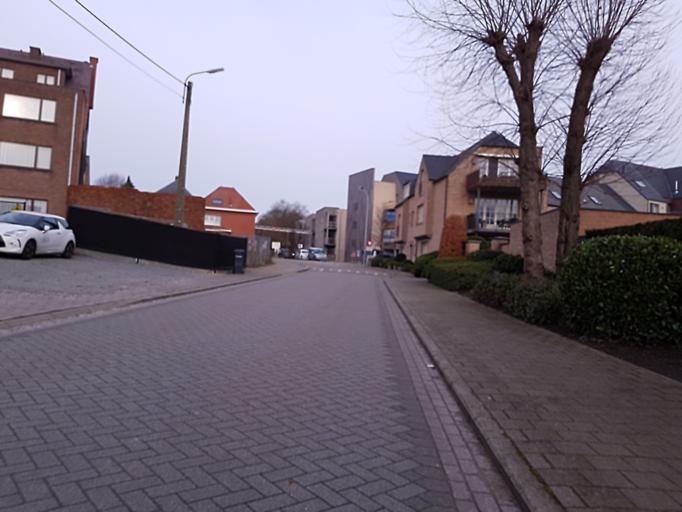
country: BE
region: Flanders
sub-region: Provincie Antwerpen
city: Putte
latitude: 51.0575
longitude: 4.6672
